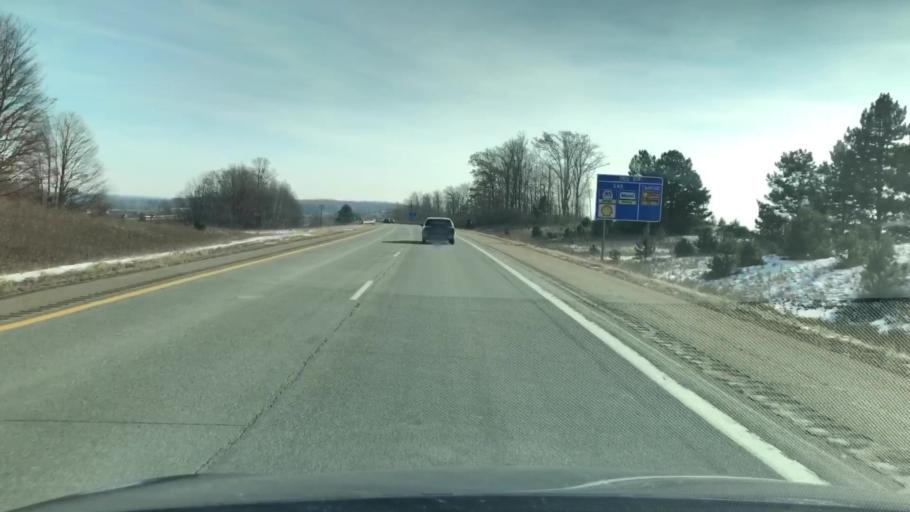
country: US
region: Michigan
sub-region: Ogemaw County
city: West Branch
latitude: 44.2502
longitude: -84.2404
